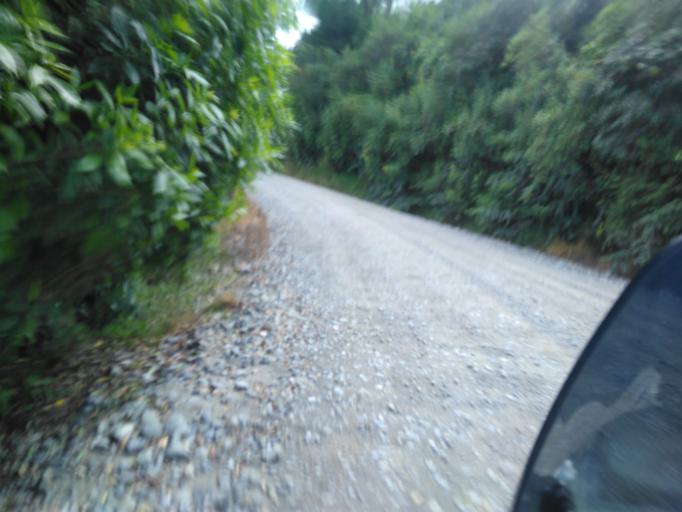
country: NZ
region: Gisborne
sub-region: Gisborne District
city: Gisborne
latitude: -38.2418
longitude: 178.0693
